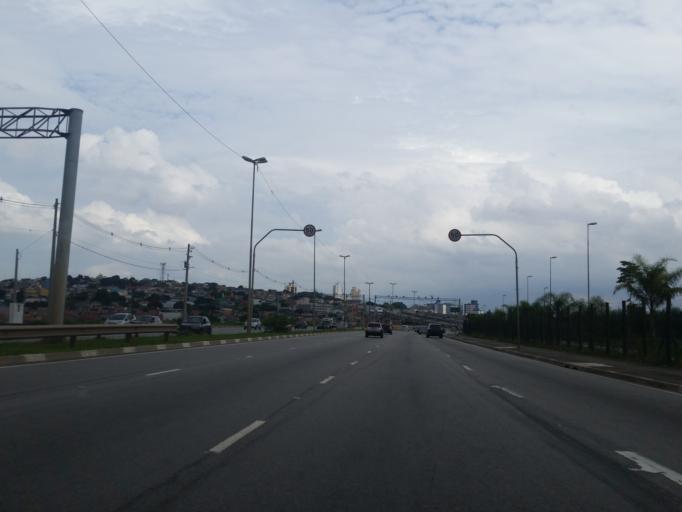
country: BR
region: Sao Paulo
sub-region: Guarulhos
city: Guarulhos
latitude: -23.4849
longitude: -46.4531
